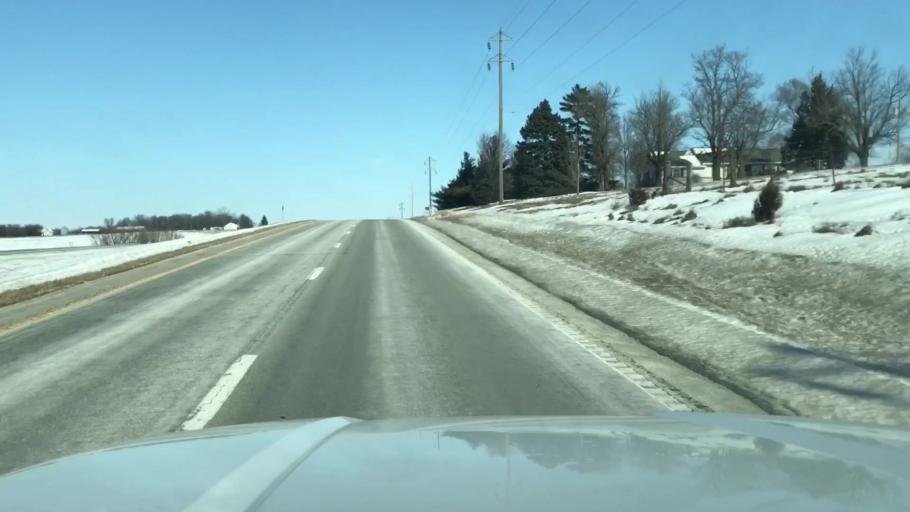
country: US
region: Missouri
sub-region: Nodaway County
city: Maryville
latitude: 40.1516
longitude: -94.8691
